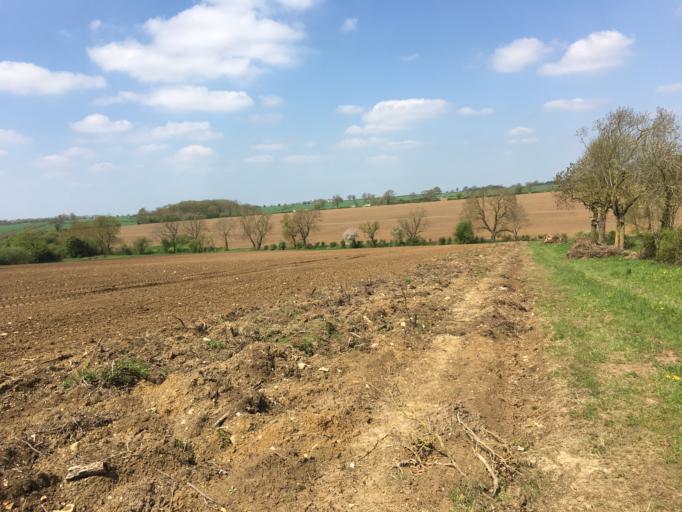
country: GB
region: England
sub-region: Leicestershire
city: Houghton on the Hill
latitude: 52.6050
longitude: -0.9921
